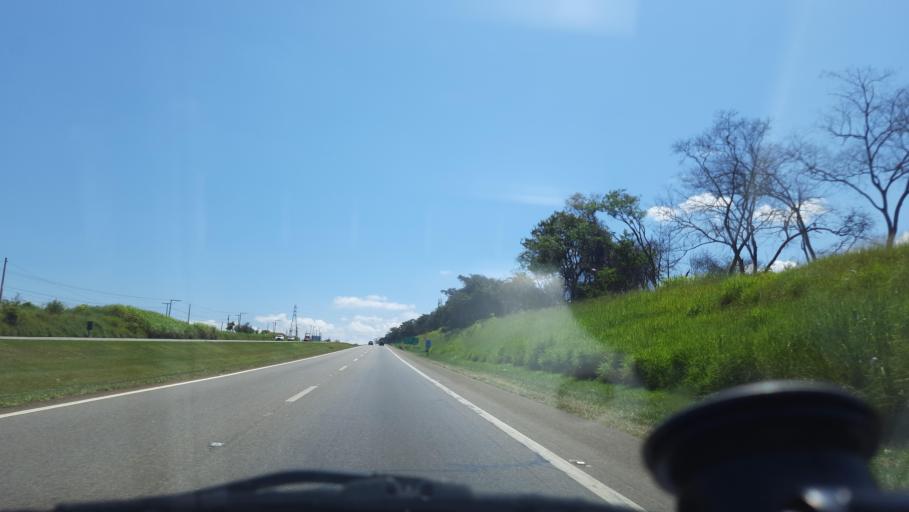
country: BR
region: Sao Paulo
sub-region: Mogi-Mirim
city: Mogi Mirim
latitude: -22.4968
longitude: -46.9833
